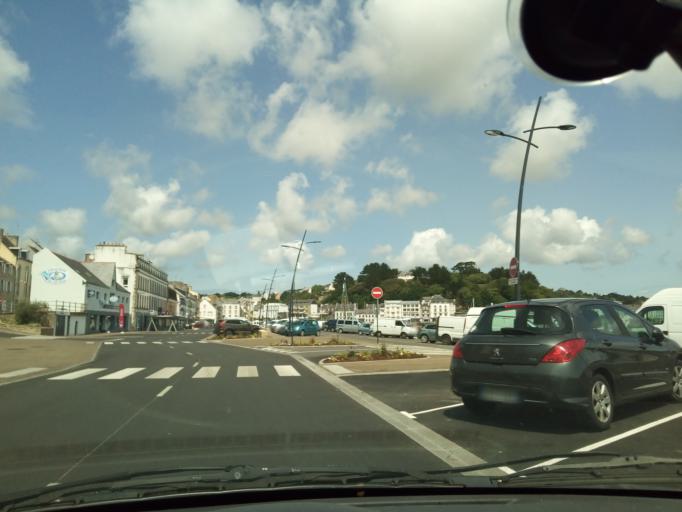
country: FR
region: Brittany
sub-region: Departement du Finistere
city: Audierne
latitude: 48.0206
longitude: -4.5365
